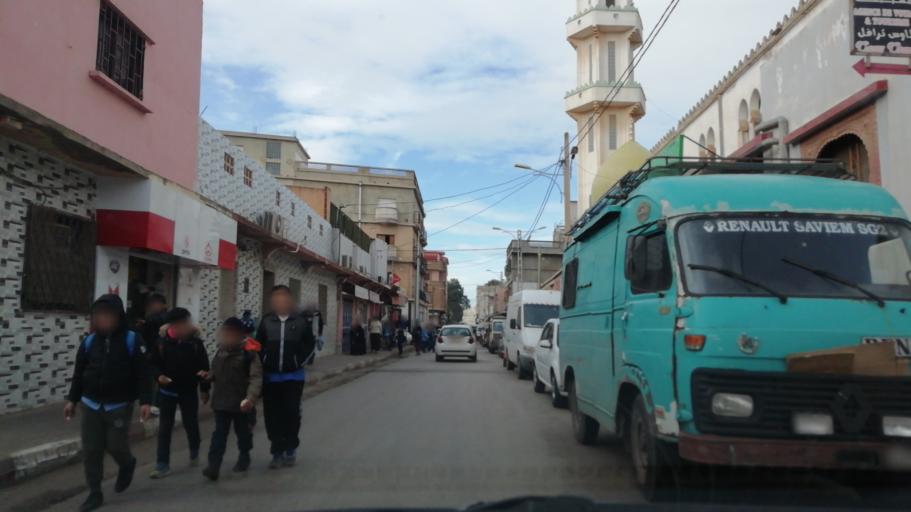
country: DZ
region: Oran
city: Oran
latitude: 35.6836
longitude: -0.6005
